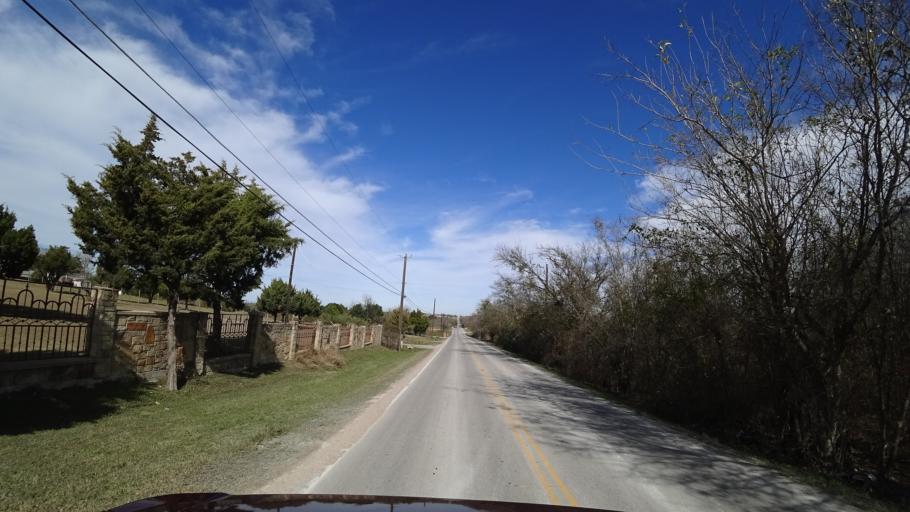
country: US
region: Texas
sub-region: Travis County
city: Onion Creek
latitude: 30.1211
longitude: -97.7428
